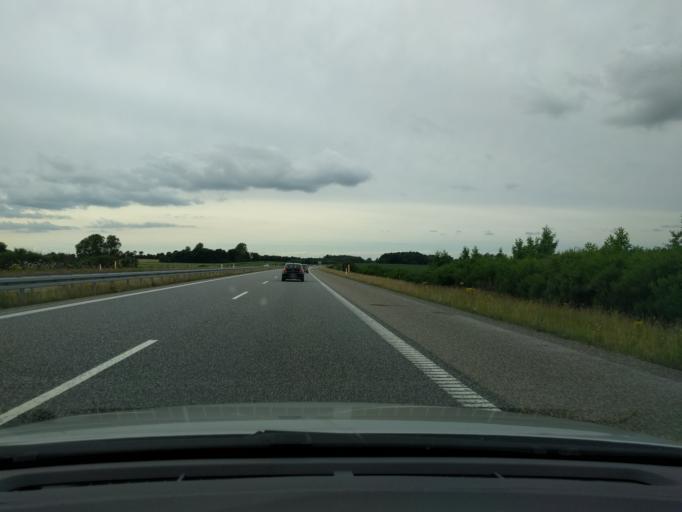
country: DK
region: South Denmark
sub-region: Vejle Kommune
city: Give
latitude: 55.8754
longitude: 9.2389
